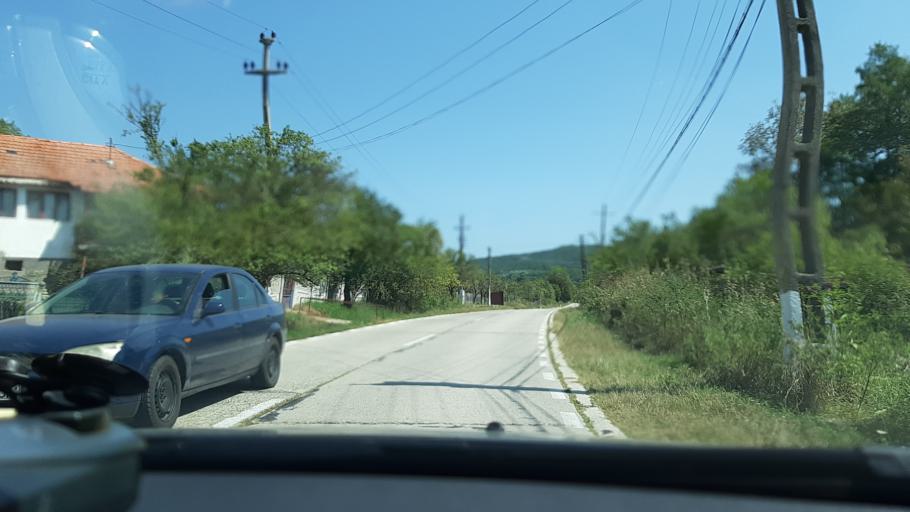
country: RO
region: Gorj
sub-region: Comuna Logresti-Mosteni
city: Logresti Mosteni
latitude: 44.9044
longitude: 23.7424
